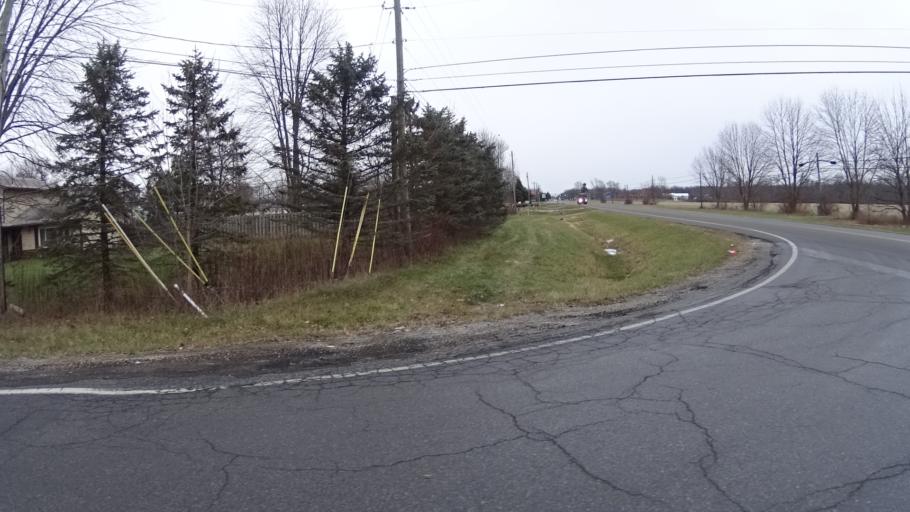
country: US
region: Ohio
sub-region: Lorain County
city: Eaton Estates
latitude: 41.3146
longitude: -82.0271
